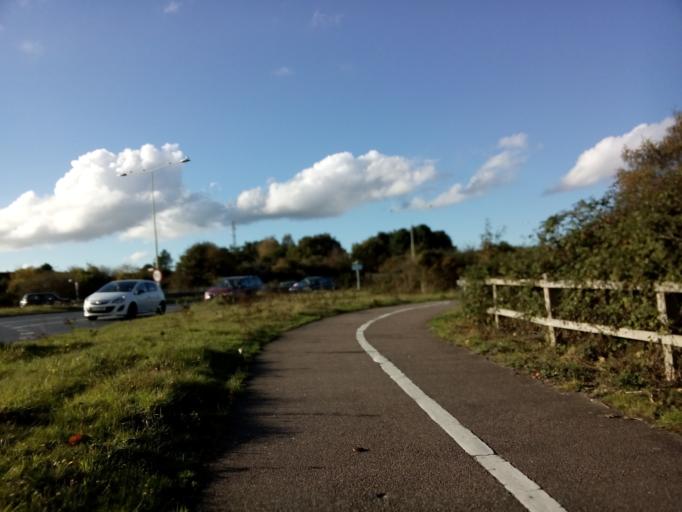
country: GB
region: England
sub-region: Suffolk
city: Kesgrave
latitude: 52.0660
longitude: 1.2751
